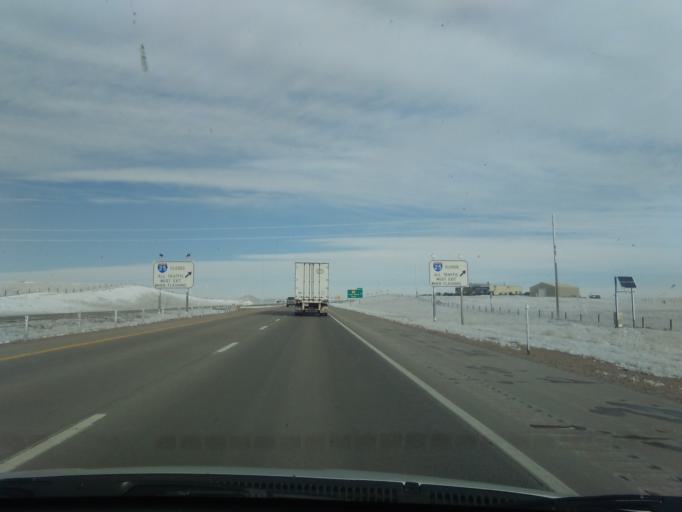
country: US
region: Wyoming
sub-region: Laramie County
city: South Greeley
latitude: 41.0284
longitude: -104.9001
